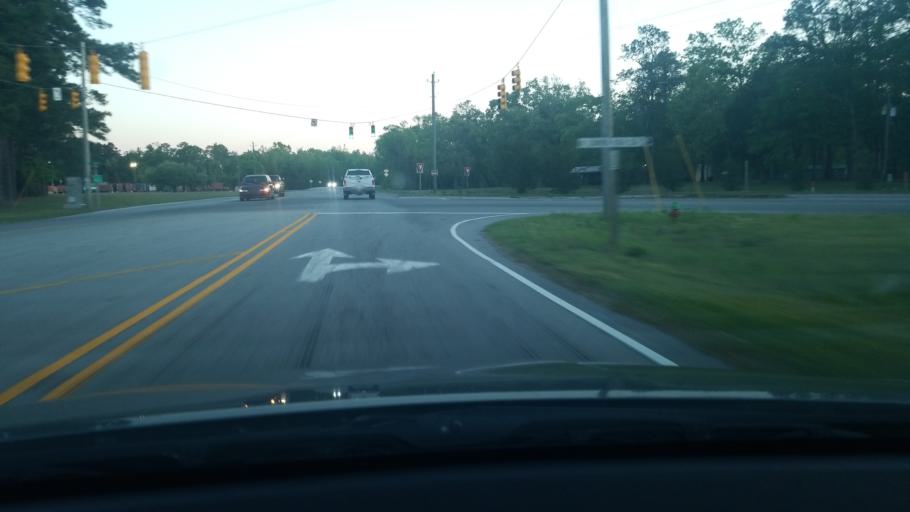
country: US
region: North Carolina
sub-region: Craven County
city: Vanceboro
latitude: 35.2170
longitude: -77.1205
